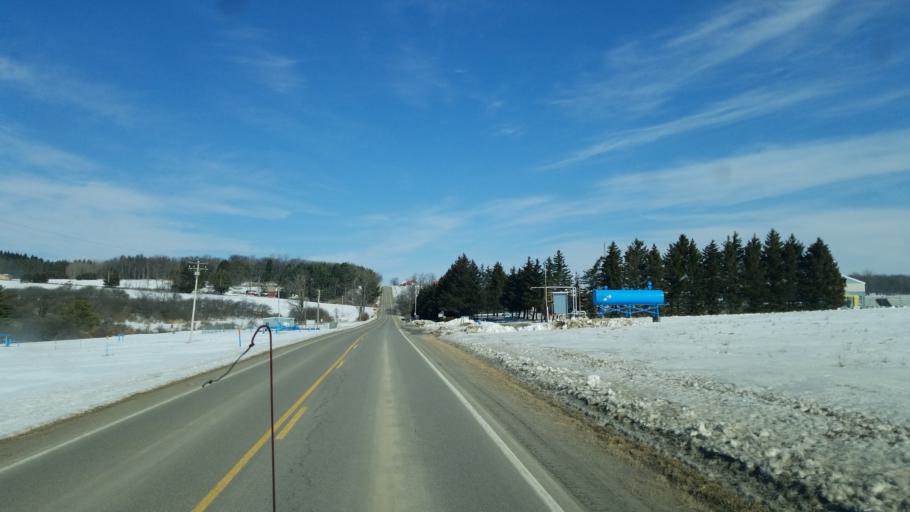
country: US
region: New York
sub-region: Allegany County
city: Andover
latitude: 42.0934
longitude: -77.7813
